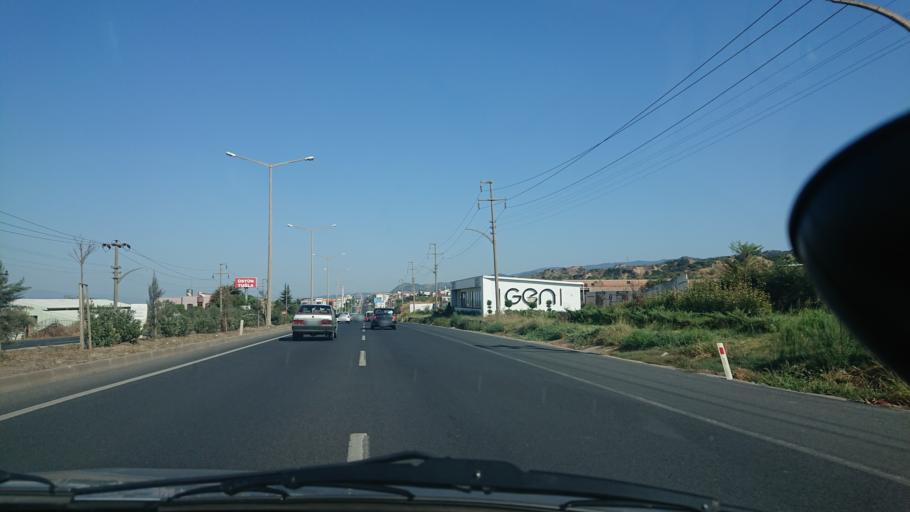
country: TR
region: Manisa
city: Turgutlu
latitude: 38.4956
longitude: 27.7471
